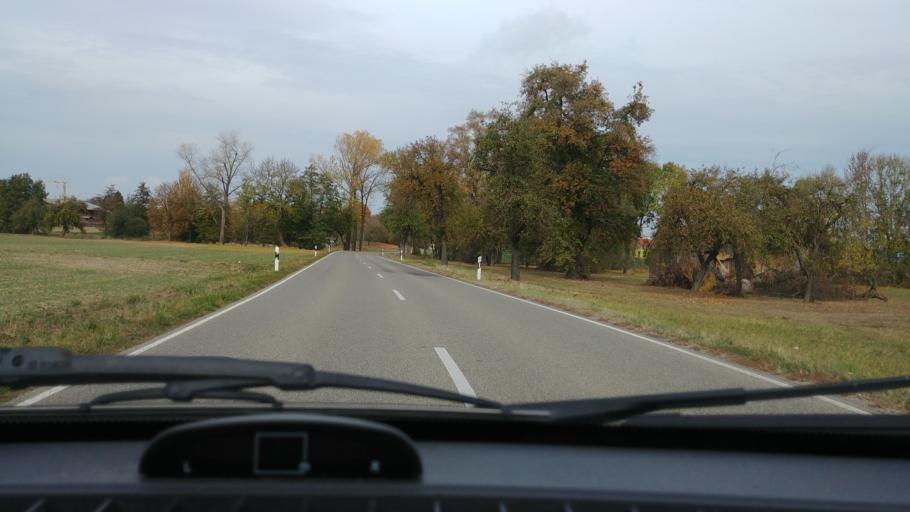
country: DE
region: Baden-Wuerttemberg
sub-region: Regierungsbezirk Stuttgart
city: Stimpfach
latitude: 49.0870
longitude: 10.0662
